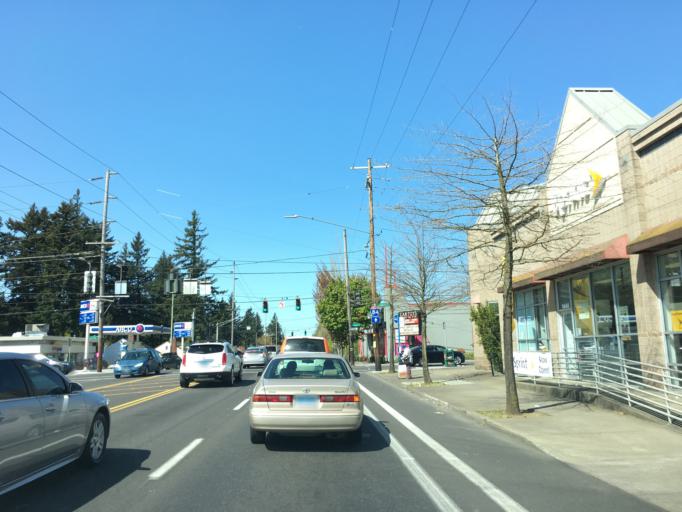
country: US
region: Oregon
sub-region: Multnomah County
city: Lents
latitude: 45.5331
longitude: -122.5580
